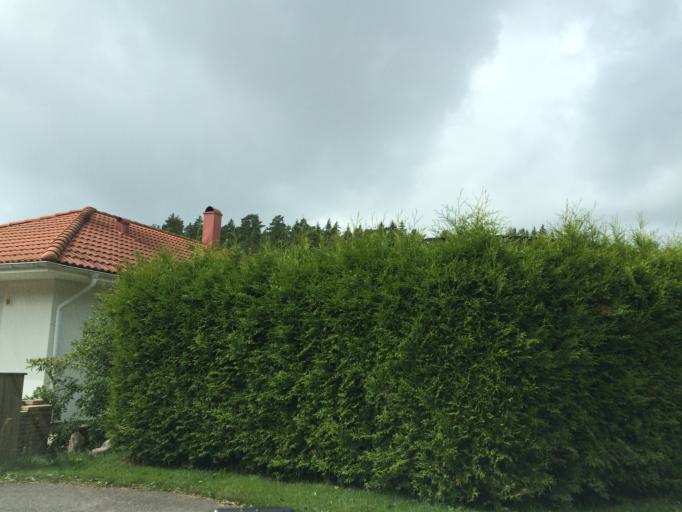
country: SE
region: Vaestra Goetaland
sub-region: Trollhattan
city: Trollhattan
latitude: 58.2984
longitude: 12.2767
